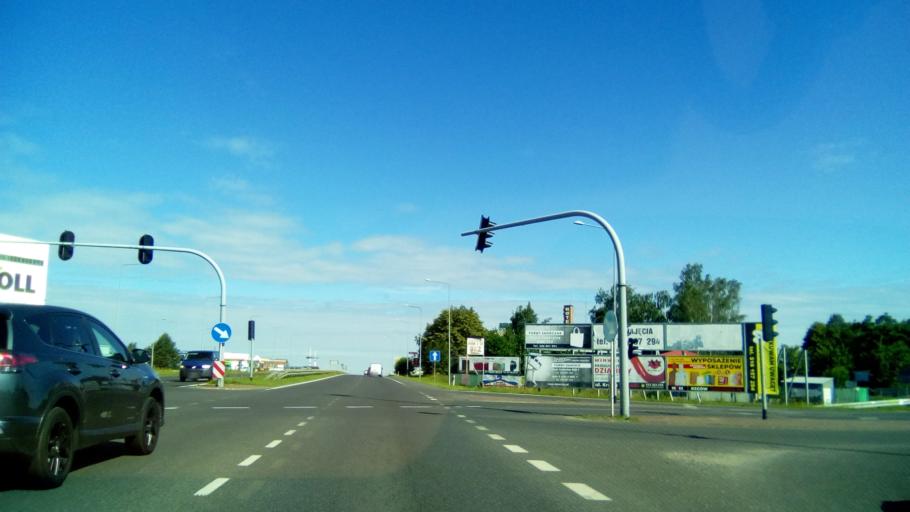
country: PL
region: Lodz Voivodeship
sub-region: Powiat lodzki wschodni
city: Rzgow
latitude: 51.6433
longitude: 19.4940
